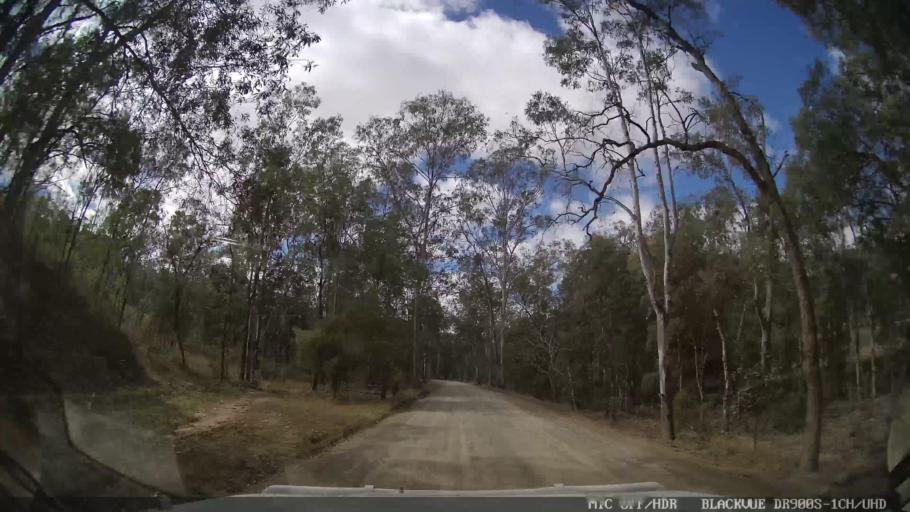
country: AU
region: Queensland
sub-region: Gladstone
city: Toolooa
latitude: -24.5512
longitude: 151.3393
